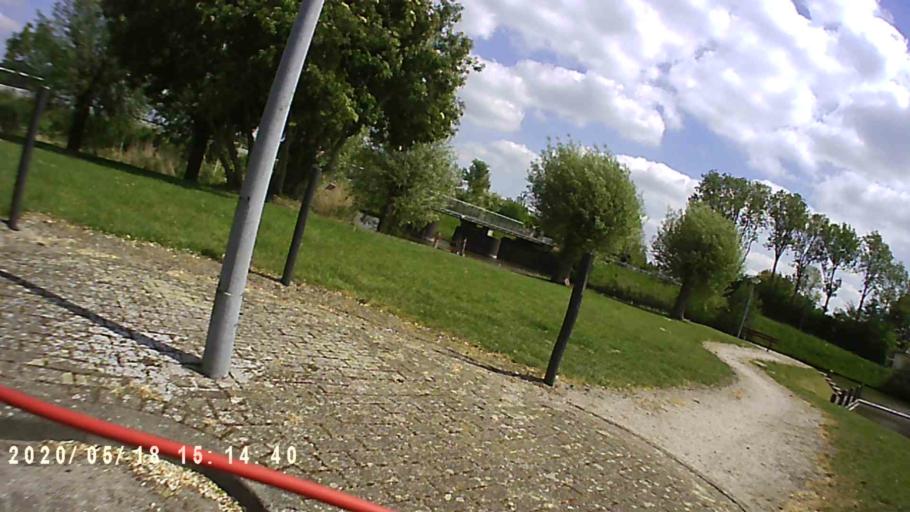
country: NL
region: Groningen
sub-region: Gemeente Winsum
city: Winsum
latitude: 53.3333
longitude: 6.5189
